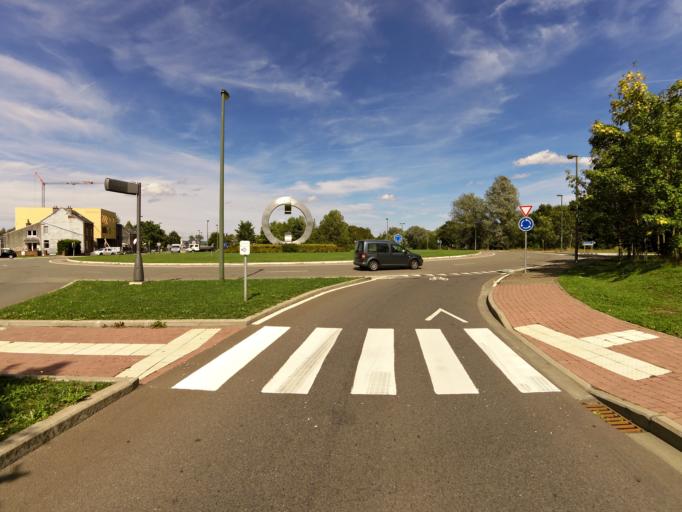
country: BE
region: Wallonia
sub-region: Province du Luxembourg
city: Marche-en-Famenne
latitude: 50.2372
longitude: 5.3448
